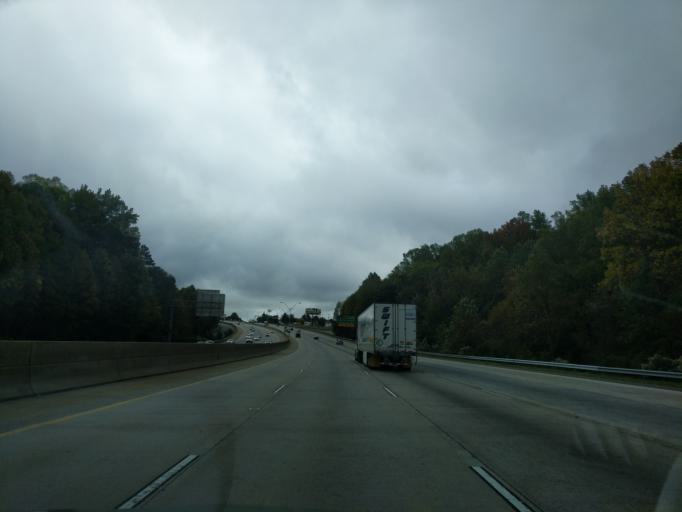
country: US
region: North Carolina
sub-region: Gaston County
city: Mount Holly
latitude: 35.2422
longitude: -80.9510
